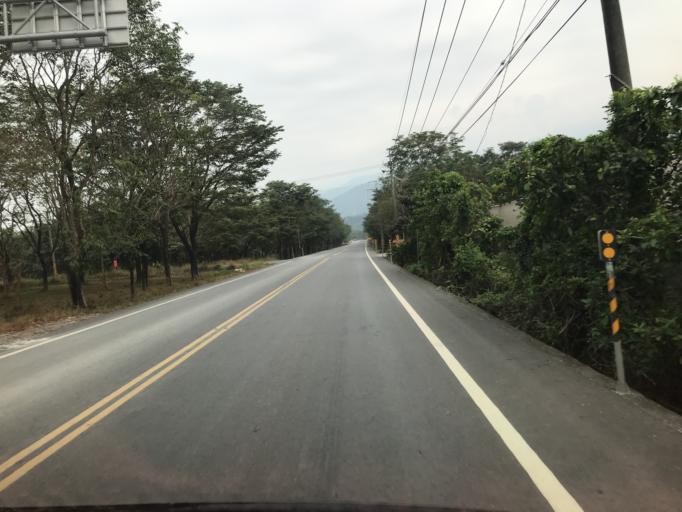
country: TW
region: Taiwan
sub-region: Pingtung
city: Pingtung
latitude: 22.4522
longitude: 120.6100
